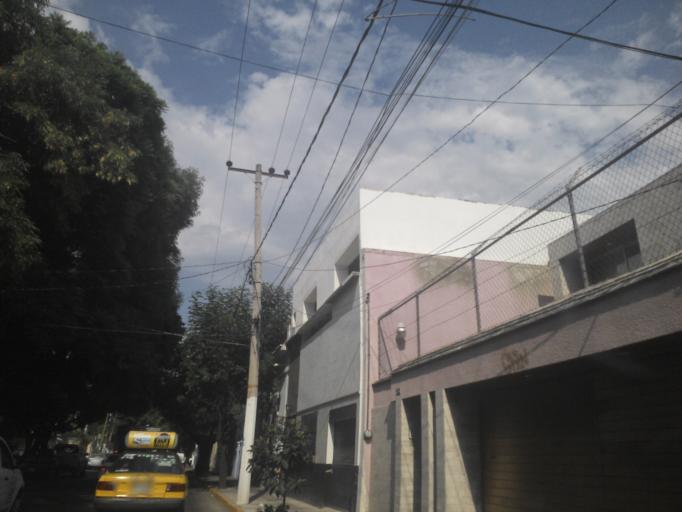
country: MX
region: Jalisco
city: Guadalajara
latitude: 20.6739
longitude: -103.3620
